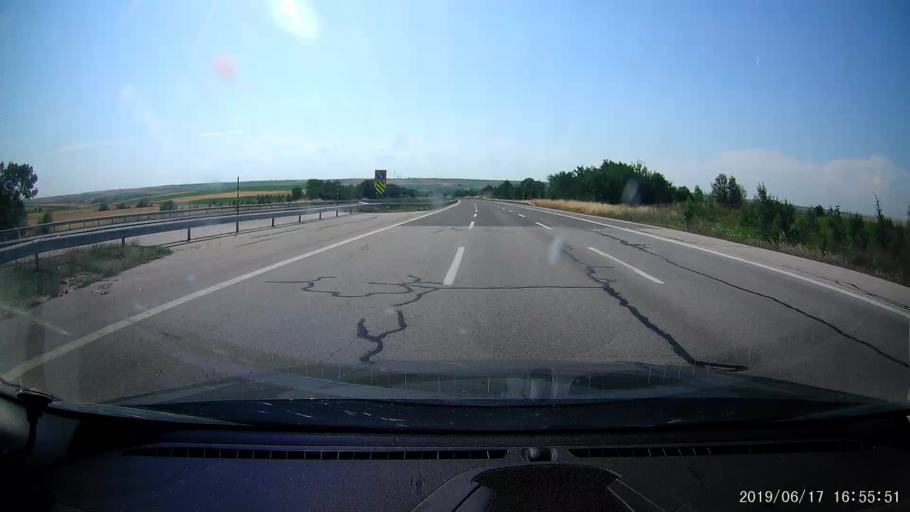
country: TR
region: Edirne
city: Haskoy
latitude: 41.5821
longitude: 26.9537
